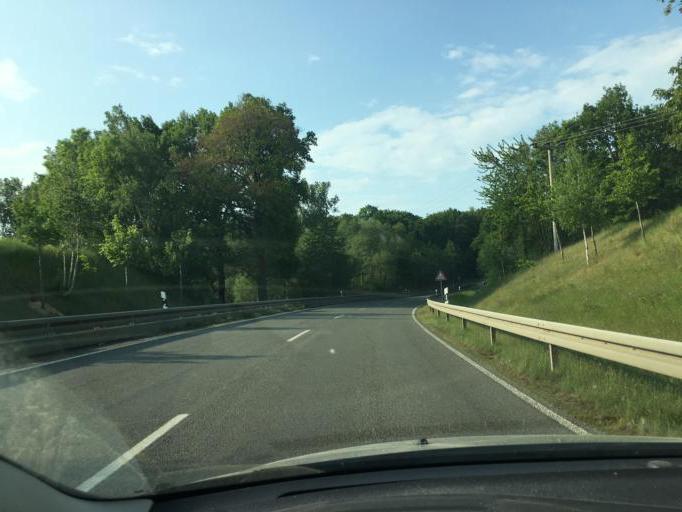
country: DE
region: Saxony
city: Grossbothen
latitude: 51.1646
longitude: 12.7599
